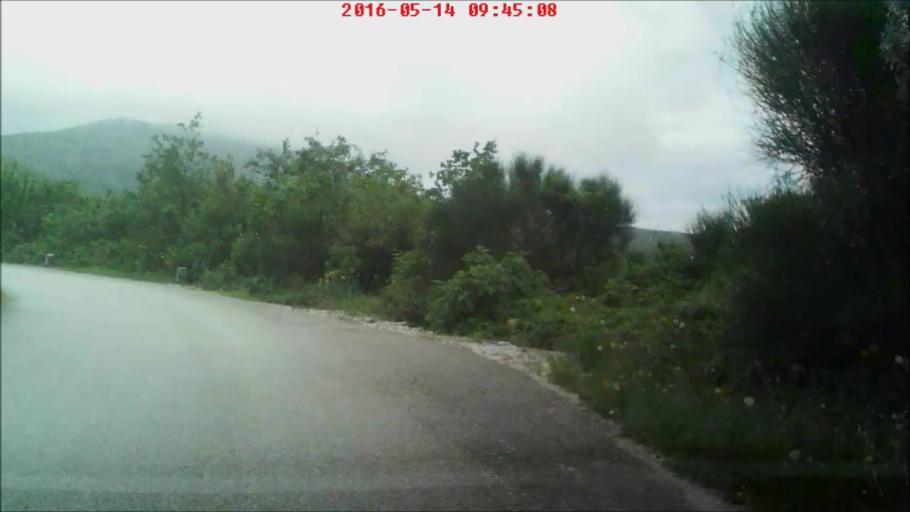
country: HR
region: Dubrovacko-Neretvanska
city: Podgora
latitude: 42.7826
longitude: 17.9104
